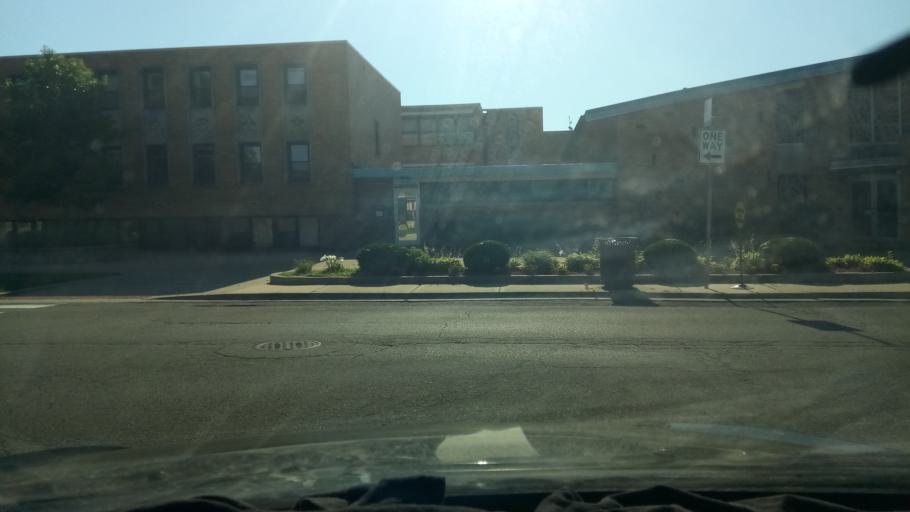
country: US
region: Illinois
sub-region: Cook County
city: Hometown
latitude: 41.7758
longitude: -87.7350
